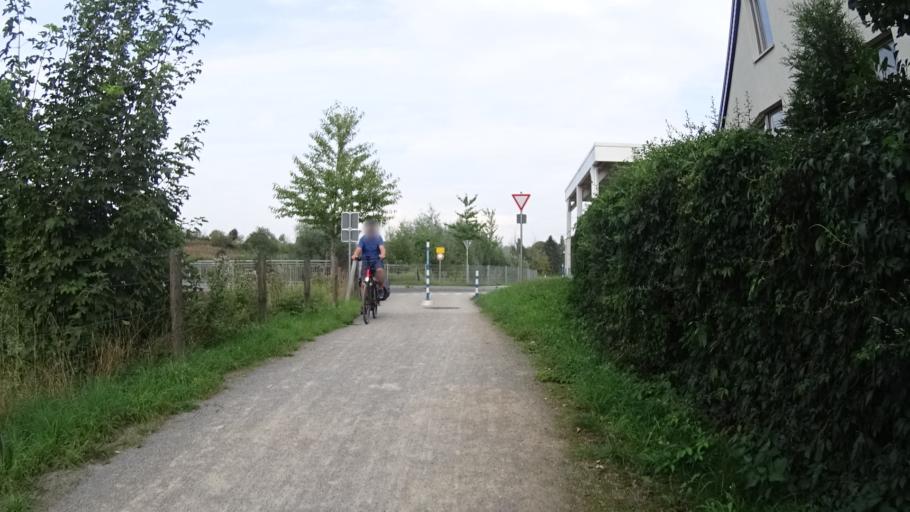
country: DE
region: North Rhine-Westphalia
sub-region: Regierungsbezirk Arnsberg
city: Dortmund
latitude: 51.4853
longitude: 7.4272
